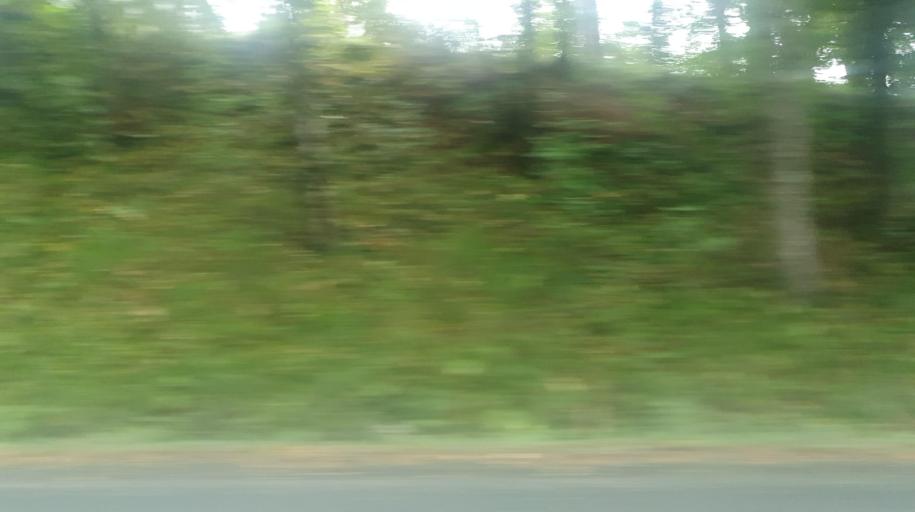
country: NO
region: Nord-Trondelag
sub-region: Verdal
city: Verdal
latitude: 63.7956
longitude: 11.5140
